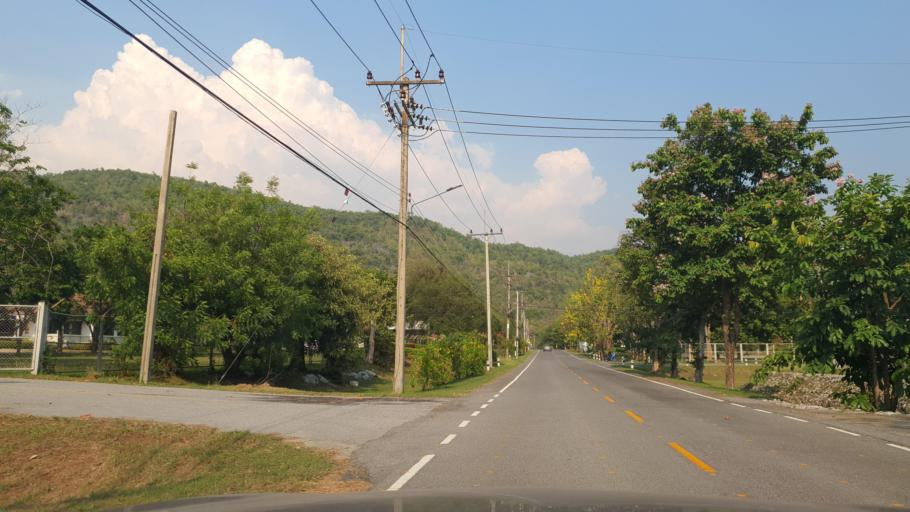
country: TH
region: Kanchanaburi
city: Sai Yok
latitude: 14.2299
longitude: 99.2342
